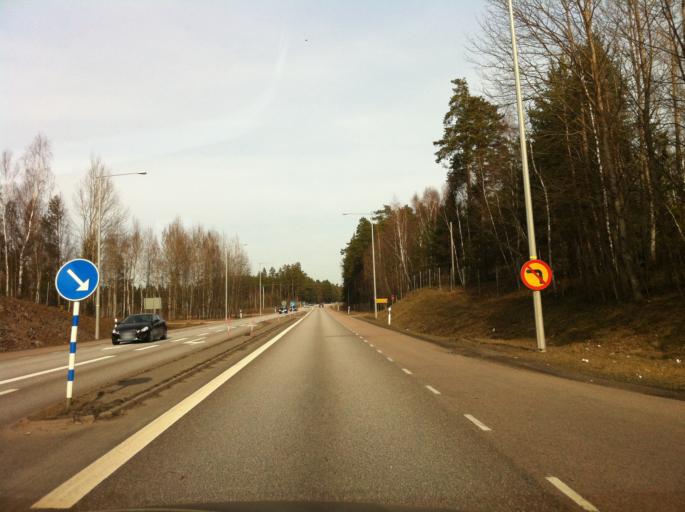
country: SE
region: Vaestra Goetaland
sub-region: Mariestads Kommun
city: Mariestad
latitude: 58.6944
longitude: 13.8597
